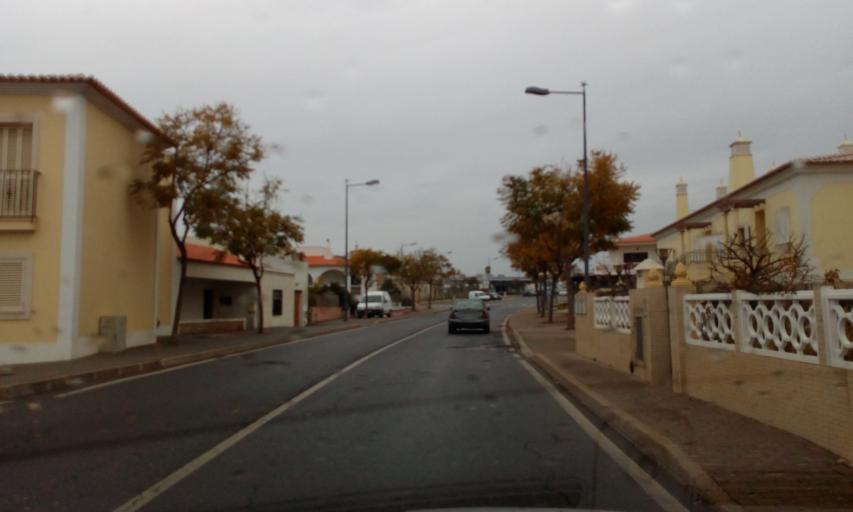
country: PT
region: Faro
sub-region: Albufeira
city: Ferreiras
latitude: 37.1071
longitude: -8.2309
